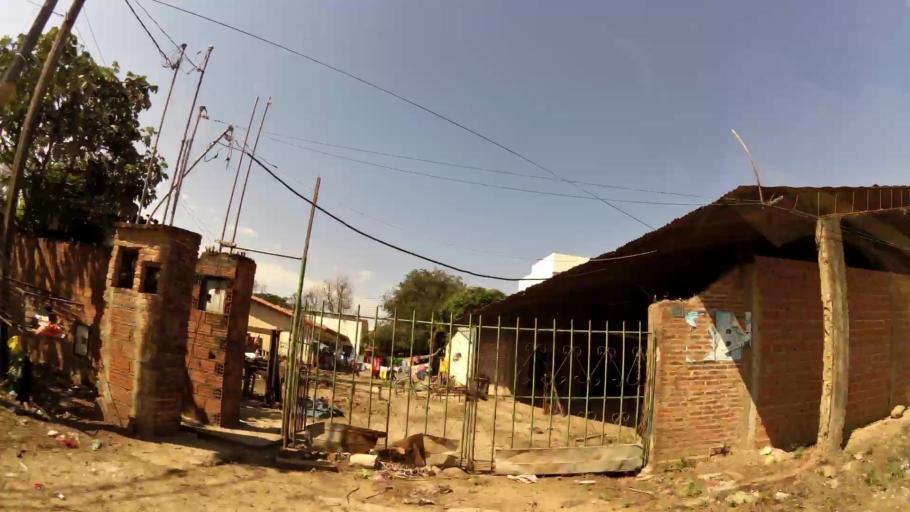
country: BO
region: Santa Cruz
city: Santa Cruz de la Sierra
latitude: -17.7304
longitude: -63.1606
